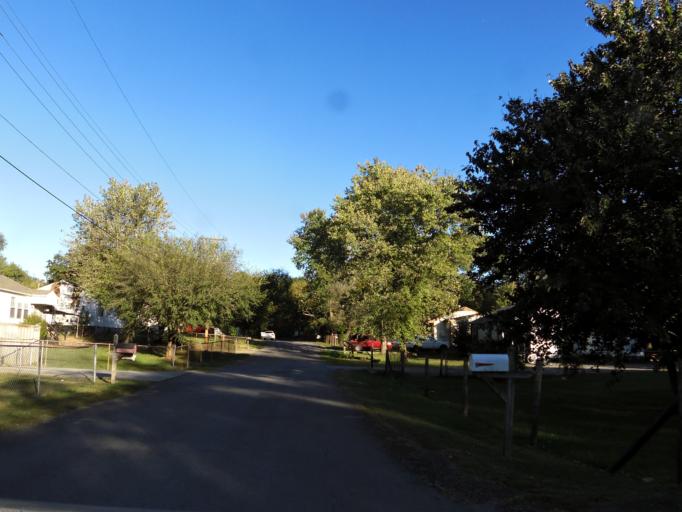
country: US
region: Tennessee
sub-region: Blount County
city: Alcoa
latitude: 35.7888
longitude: -83.9536
